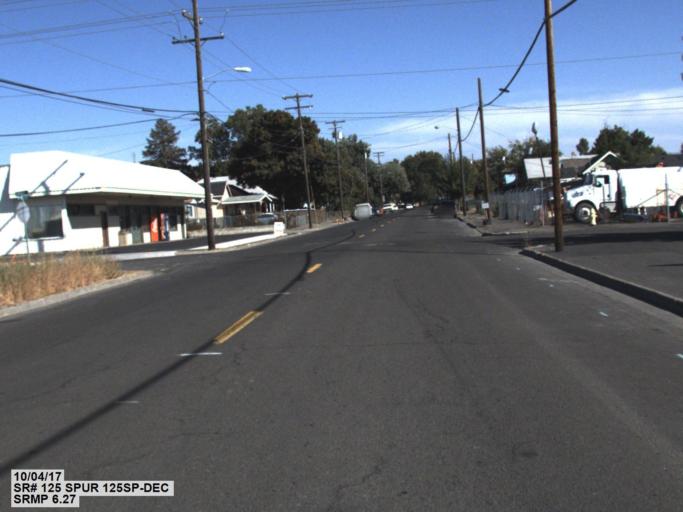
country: US
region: Washington
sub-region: Walla Walla County
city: College Place
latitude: 46.0033
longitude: -118.3880
